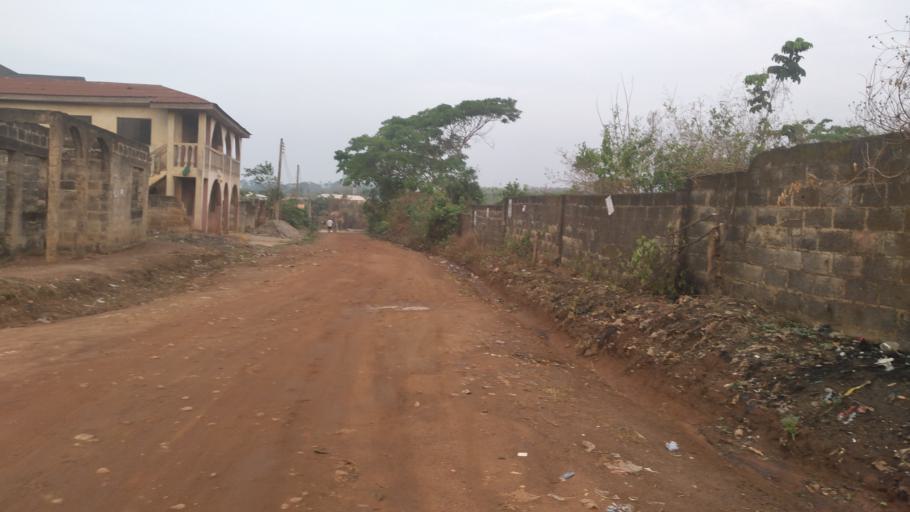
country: NG
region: Ondo
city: Akure
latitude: 7.2959
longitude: 5.1555
